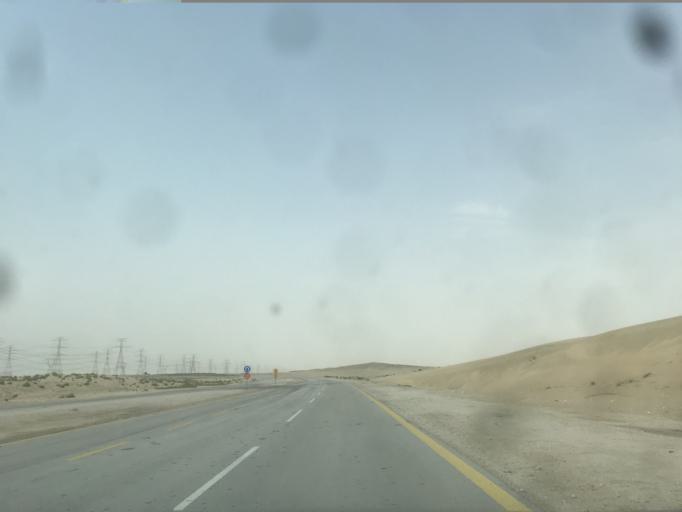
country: SA
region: Eastern Province
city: Abqaiq
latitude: 25.9076
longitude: 49.9031
